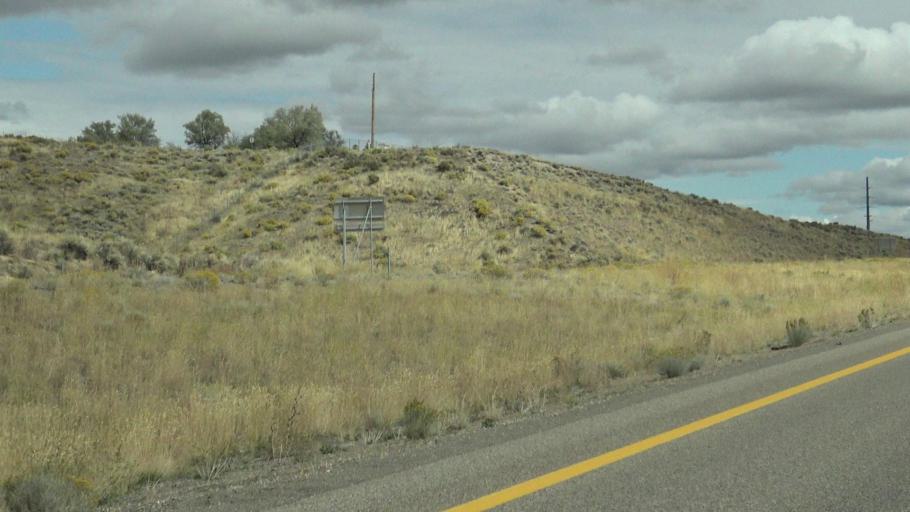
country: US
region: Nevada
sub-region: Elko County
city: Elko
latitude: 40.8568
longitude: -115.7422
